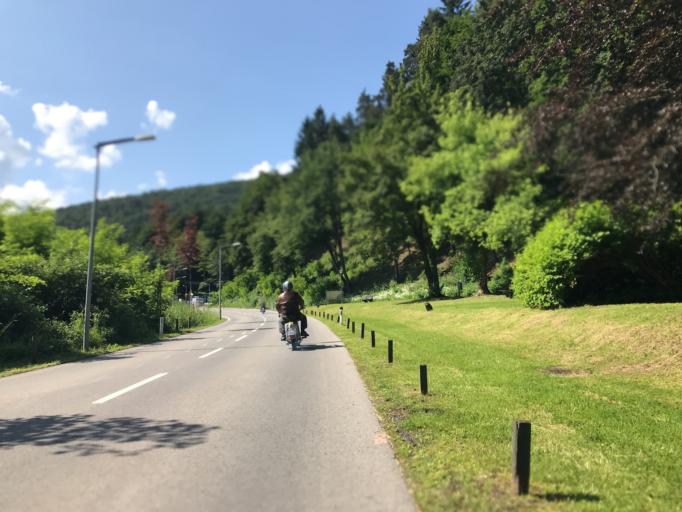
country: AT
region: Carinthia
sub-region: Villach Stadt
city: Villach
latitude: 46.5857
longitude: 13.8273
